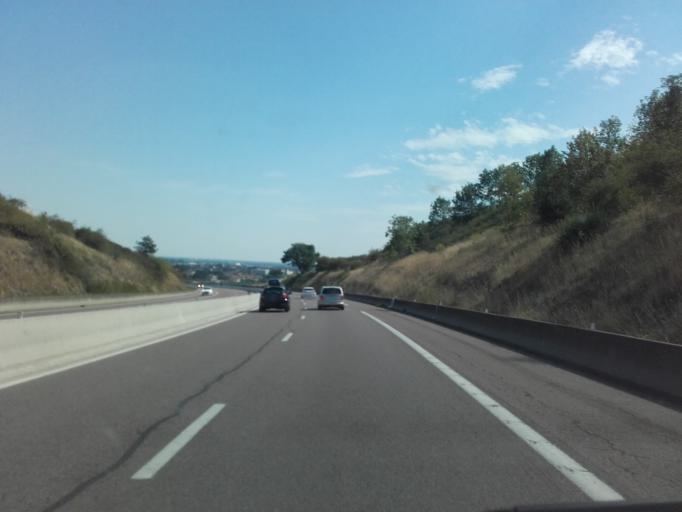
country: FR
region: Bourgogne
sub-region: Departement de la Cote-d'Or
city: Beaune
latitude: 47.0503
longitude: 4.8306
